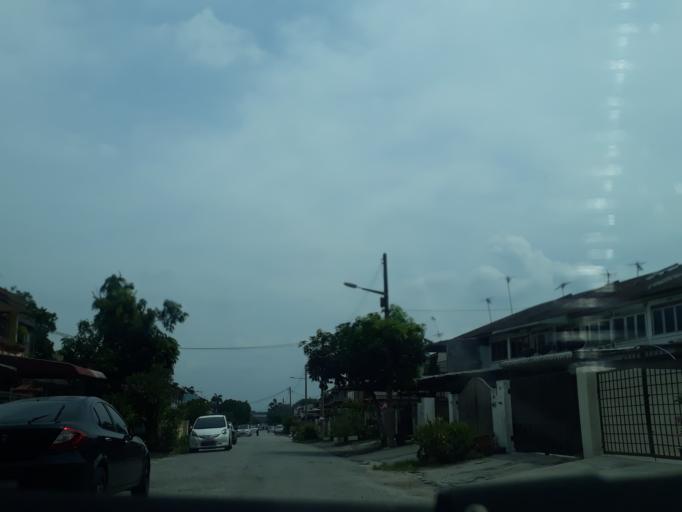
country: MY
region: Perak
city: Ipoh
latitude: 4.5939
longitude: 101.1336
